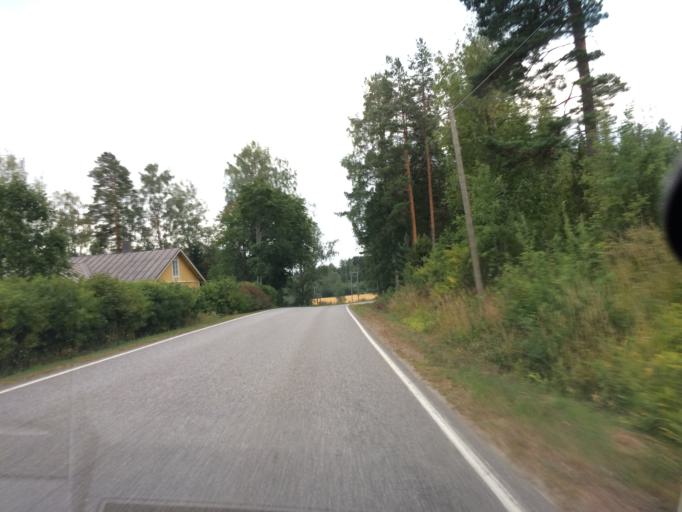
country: FI
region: Haeme
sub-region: Haemeenlinna
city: Tuulos
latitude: 61.2165
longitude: 24.7308
